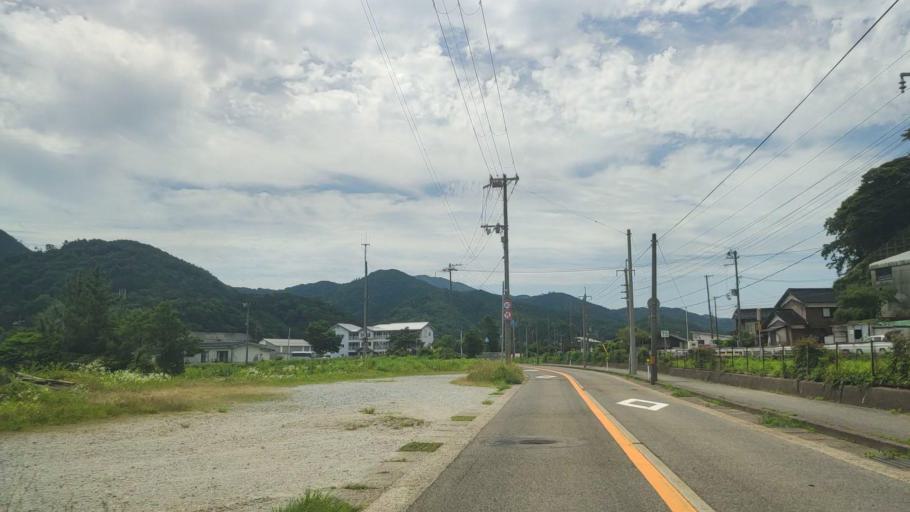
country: JP
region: Hyogo
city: Toyooka
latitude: 35.6484
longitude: 134.7577
